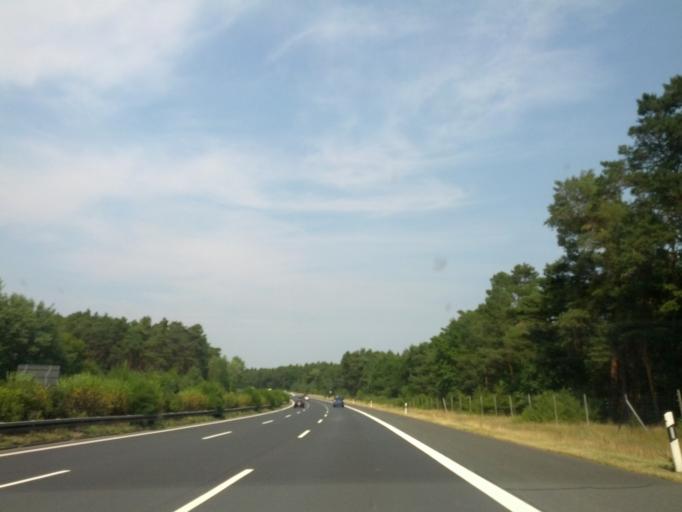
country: DE
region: Brandenburg
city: Beelitz
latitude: 52.2311
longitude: 12.9158
